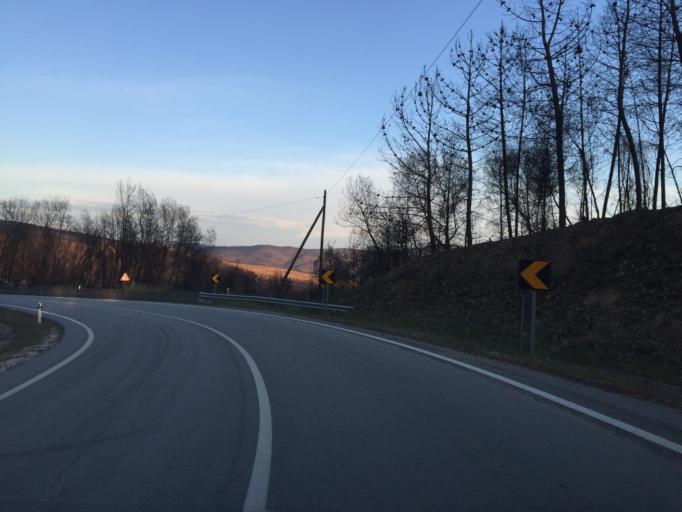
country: PT
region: Coimbra
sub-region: Pampilhosa da Serra
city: Pampilhosa da Serra
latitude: 40.0687
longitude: -7.9752
